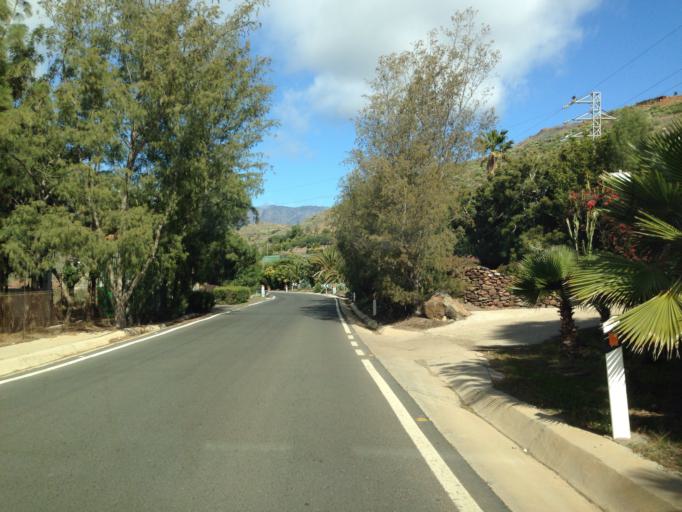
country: ES
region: Canary Islands
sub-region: Provincia de Las Palmas
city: Santa Lucia
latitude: 27.8679
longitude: -15.5646
